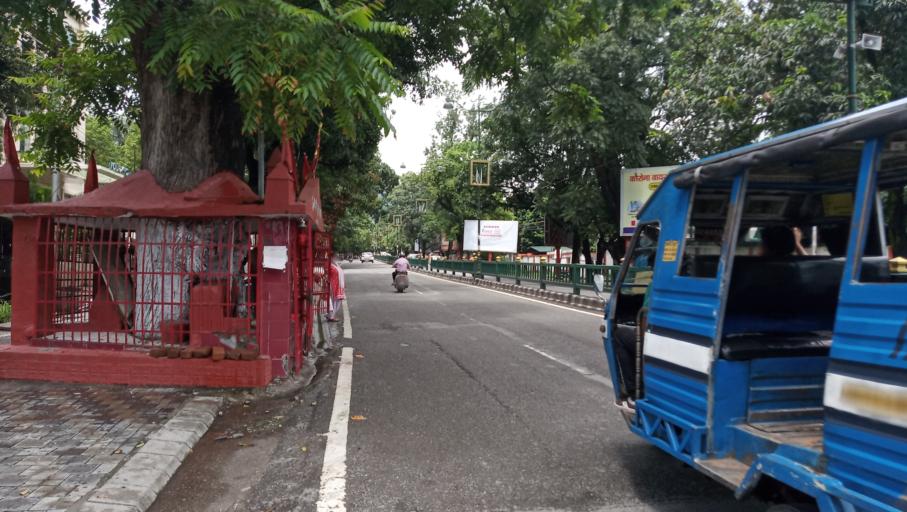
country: IN
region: Uttarakhand
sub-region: Dehradun
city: Dehradun
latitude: 30.3648
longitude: 78.0700
